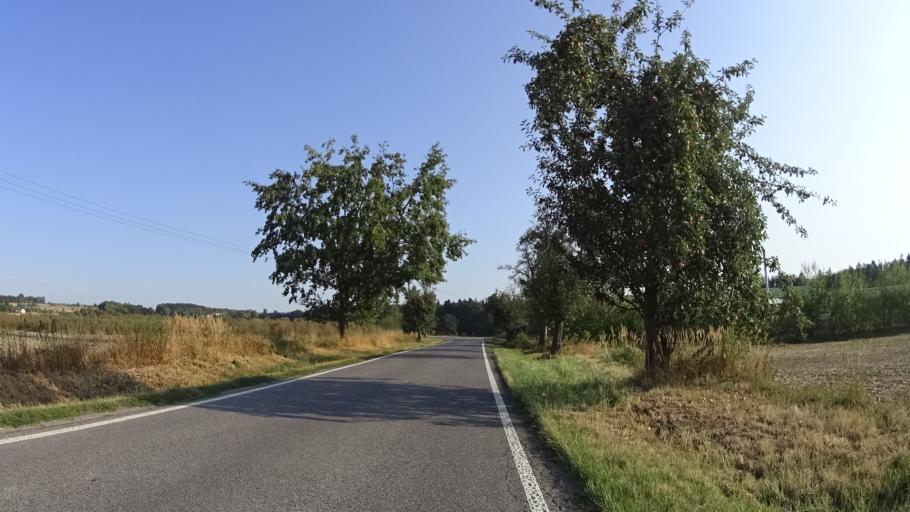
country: CZ
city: Ohrazenice
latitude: 50.6139
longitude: 15.1267
